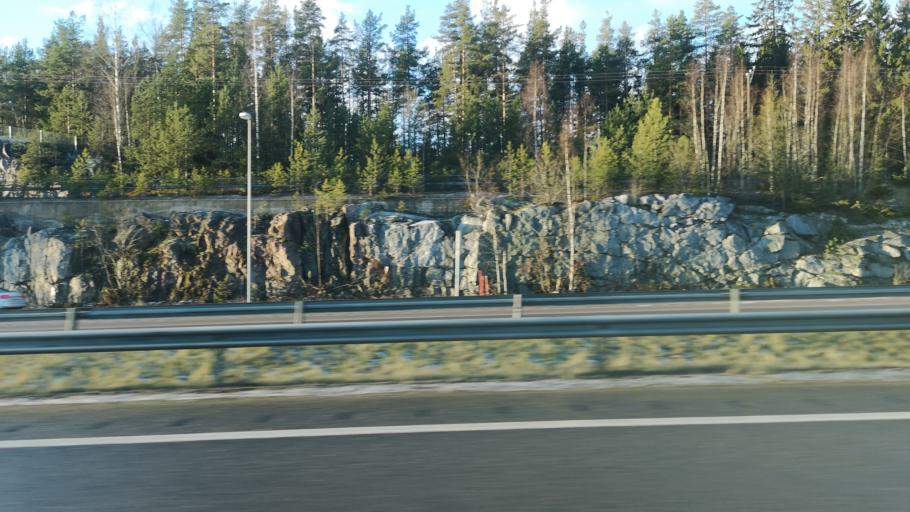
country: FI
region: Paijanne Tavastia
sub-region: Lahti
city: Heinola
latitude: 61.1964
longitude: 26.0030
